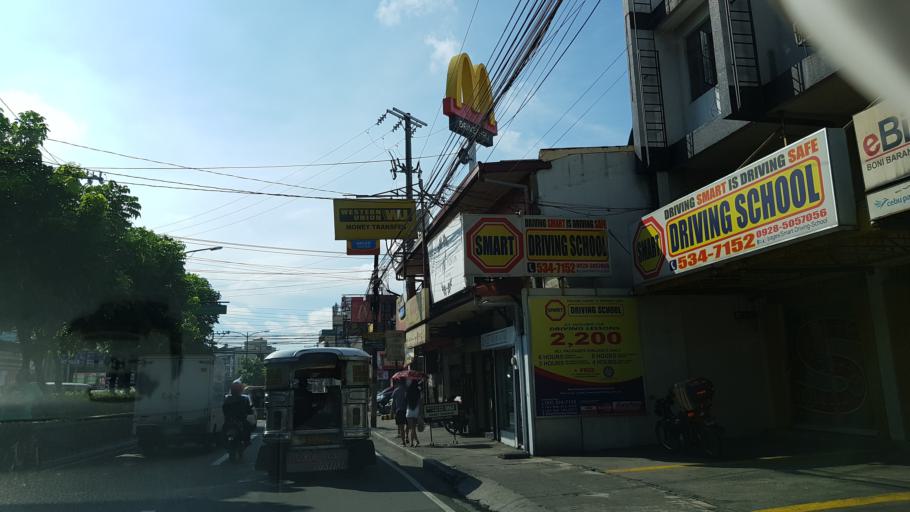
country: PH
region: Metro Manila
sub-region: Mandaluyong
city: Mandaluyong City
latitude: 14.5756
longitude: 121.0416
